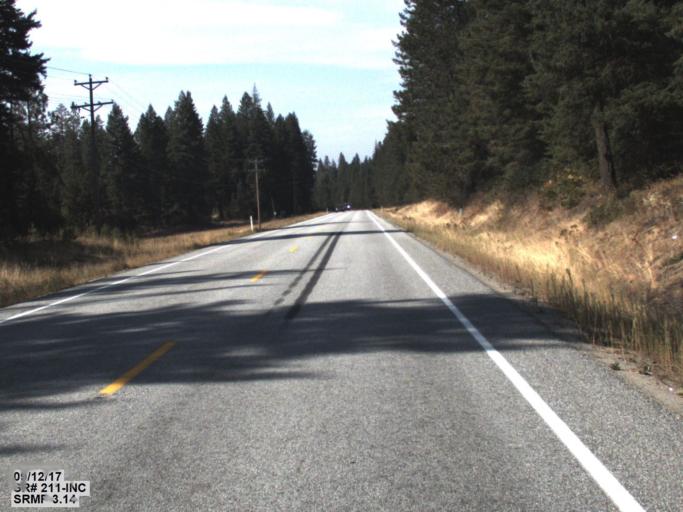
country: US
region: Washington
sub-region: Pend Oreille County
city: Newport
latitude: 48.1389
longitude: -117.2877
